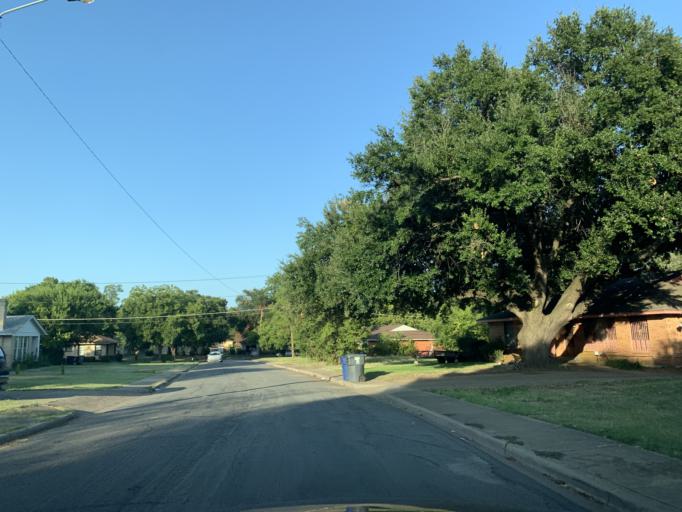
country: US
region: Texas
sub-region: Dallas County
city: Dallas
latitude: 32.7127
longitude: -96.7997
